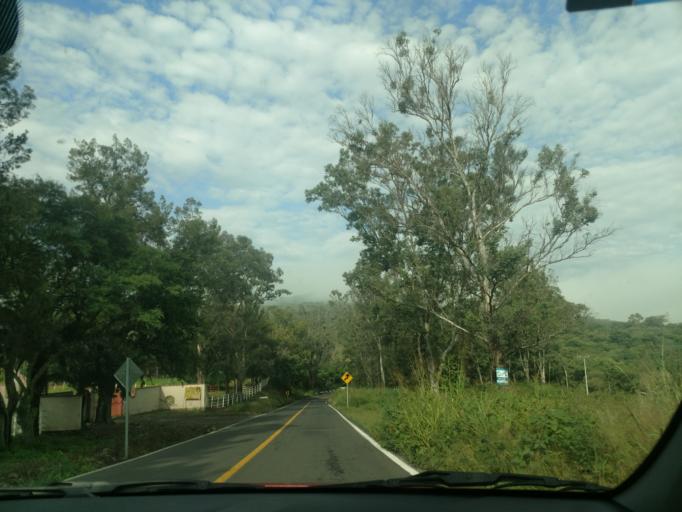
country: MX
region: Jalisco
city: Ameca
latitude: 20.5289
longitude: -104.1290
